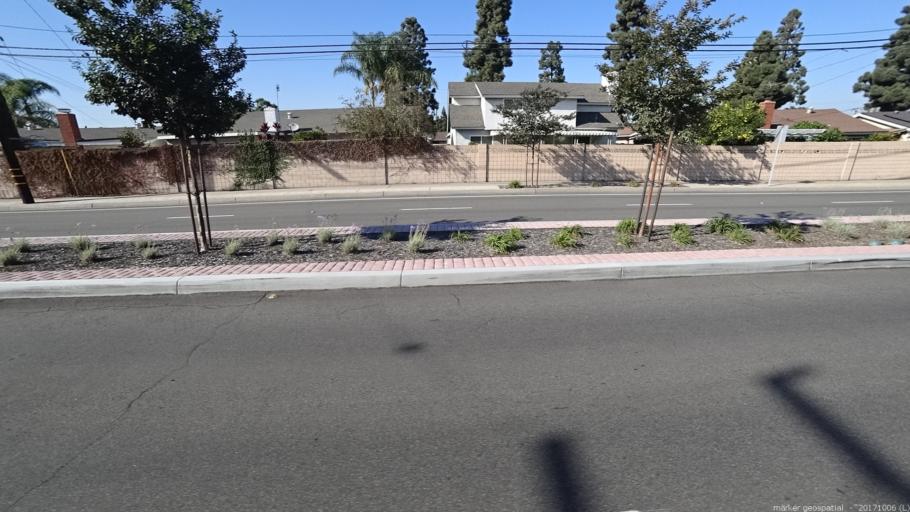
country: US
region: California
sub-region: Orange County
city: Cypress
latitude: 33.7824
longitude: -118.0371
